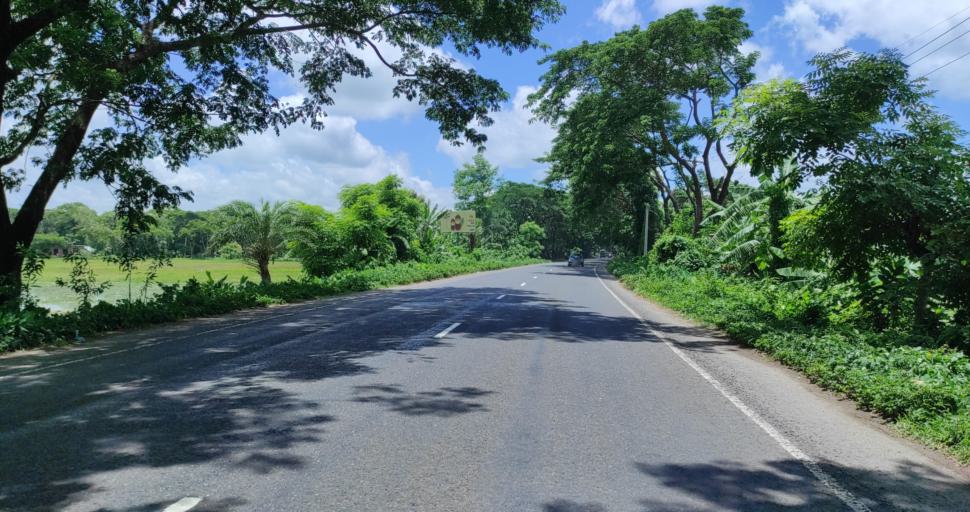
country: BD
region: Barisal
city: Barisal
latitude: 22.8215
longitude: 90.2680
